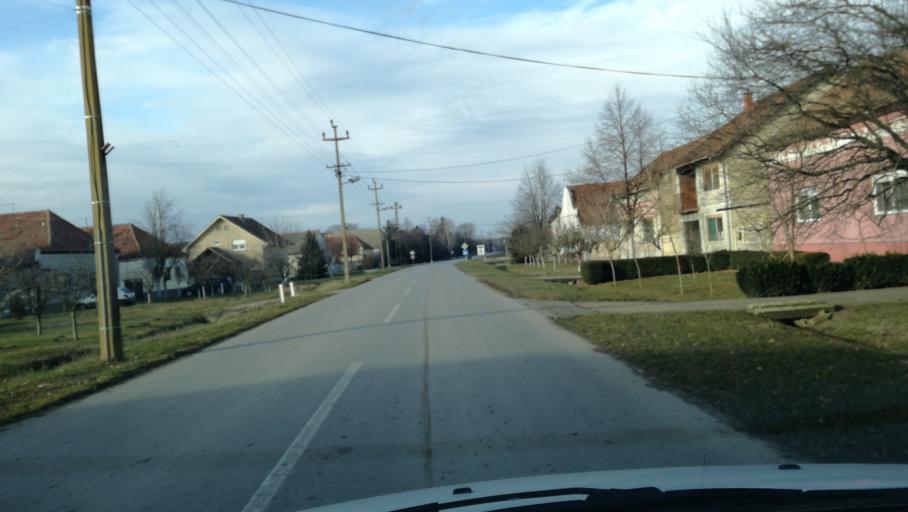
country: RS
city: Banatsko Veliko Selo
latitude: 45.8132
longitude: 20.6106
